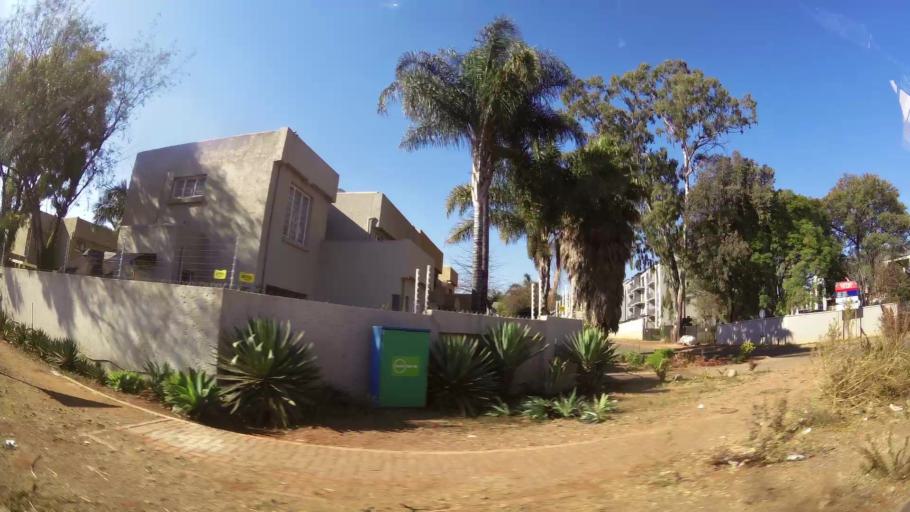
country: ZA
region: Gauteng
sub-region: City of Tshwane Metropolitan Municipality
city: Centurion
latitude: -25.8402
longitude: 28.1782
